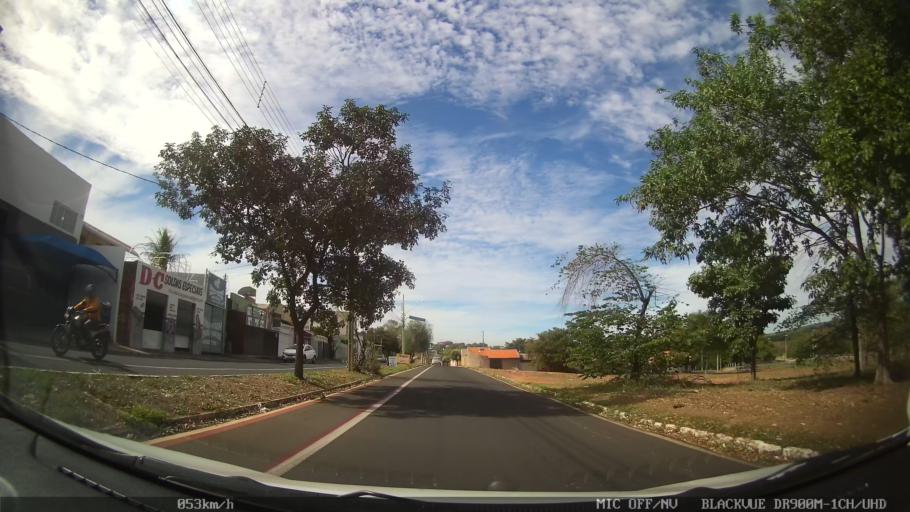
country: BR
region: Sao Paulo
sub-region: Catanduva
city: Catanduva
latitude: -21.1418
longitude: -48.9522
